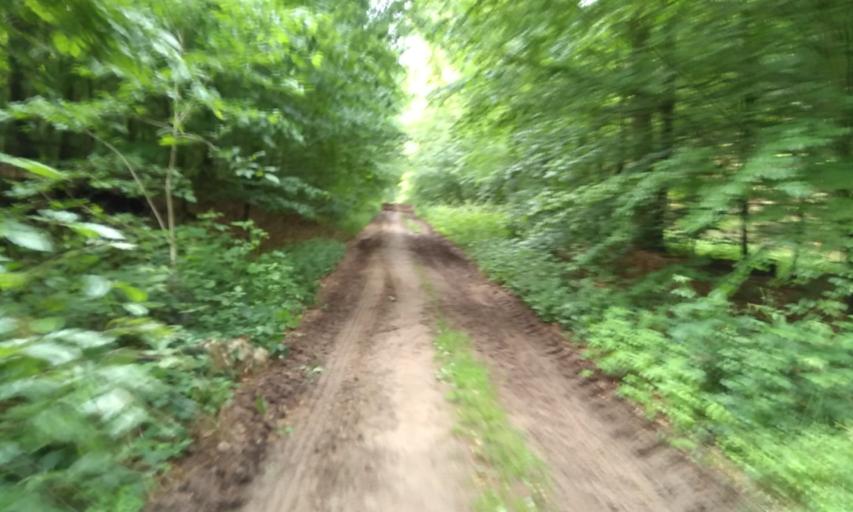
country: DE
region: Lower Saxony
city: Nottensdorf
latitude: 53.4711
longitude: 9.6221
